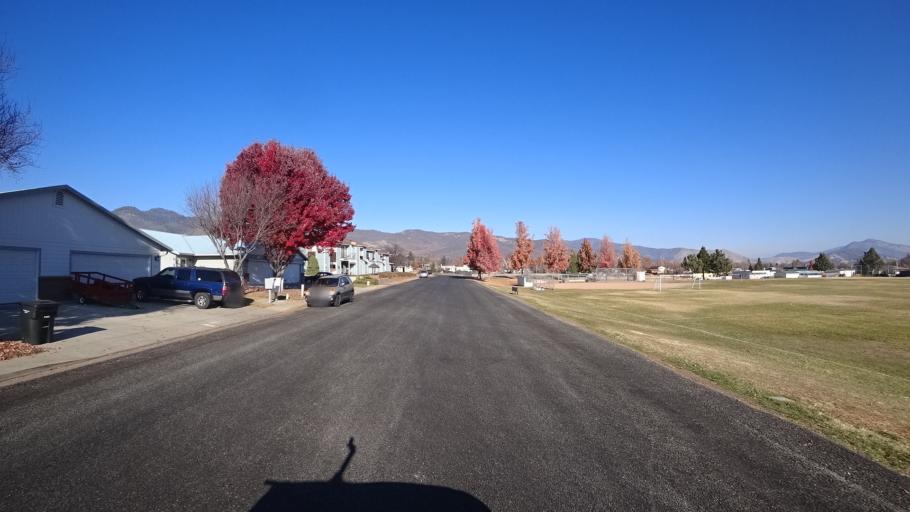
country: US
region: California
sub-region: Siskiyou County
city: Yreka
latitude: 41.7249
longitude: -122.6457
